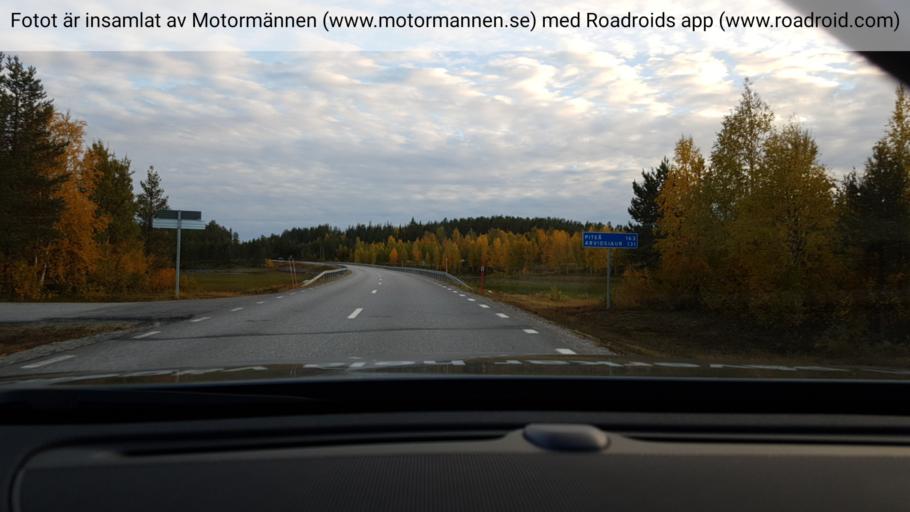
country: SE
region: Norrbotten
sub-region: Jokkmokks Kommun
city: Jokkmokk
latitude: 66.4265
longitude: 19.6821
